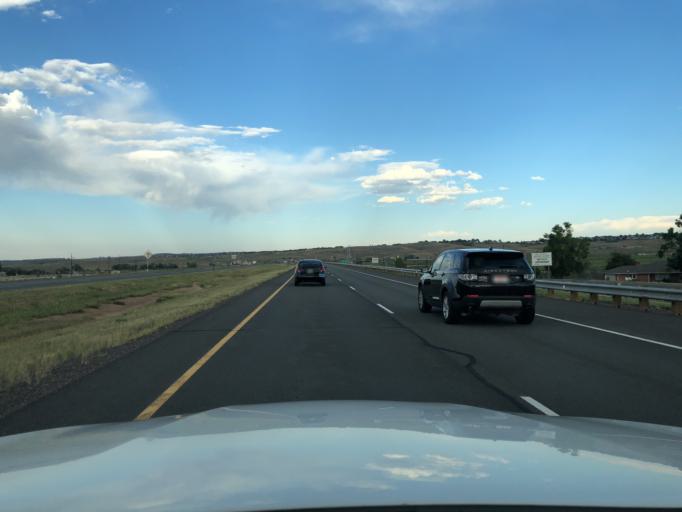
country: US
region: Colorado
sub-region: Boulder County
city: Louisville
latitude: 39.9581
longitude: -105.1013
